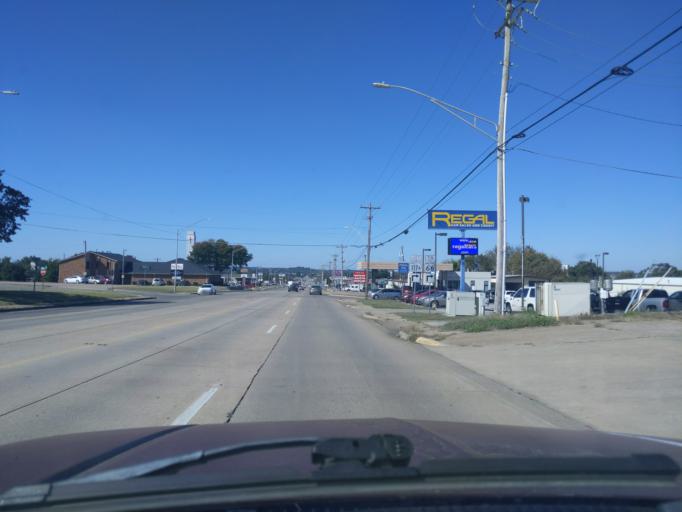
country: US
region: Oklahoma
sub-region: Creek County
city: Sapulpa
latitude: 35.9885
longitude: -96.0958
